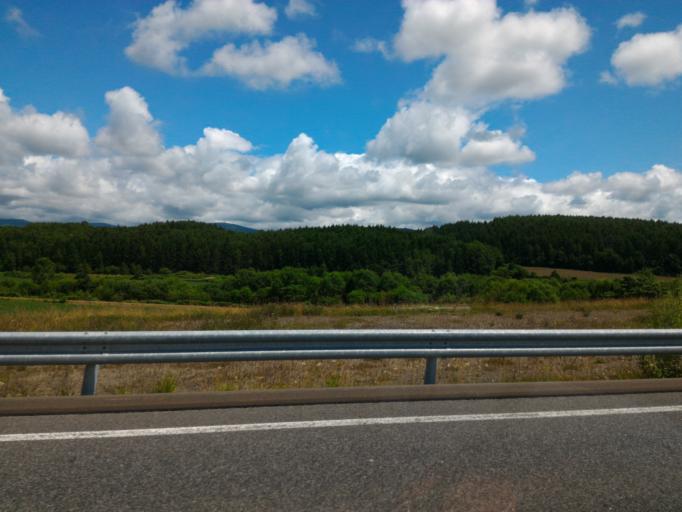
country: JP
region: Hokkaido
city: Nayoro
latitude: 44.4154
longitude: 142.4028
